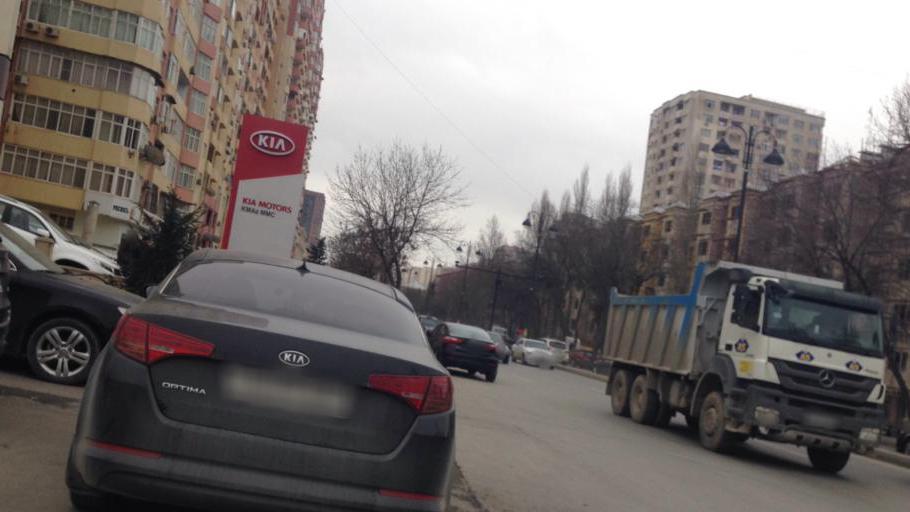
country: AZ
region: Baki
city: Khodzhi-Gasan
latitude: 40.3885
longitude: 49.8079
